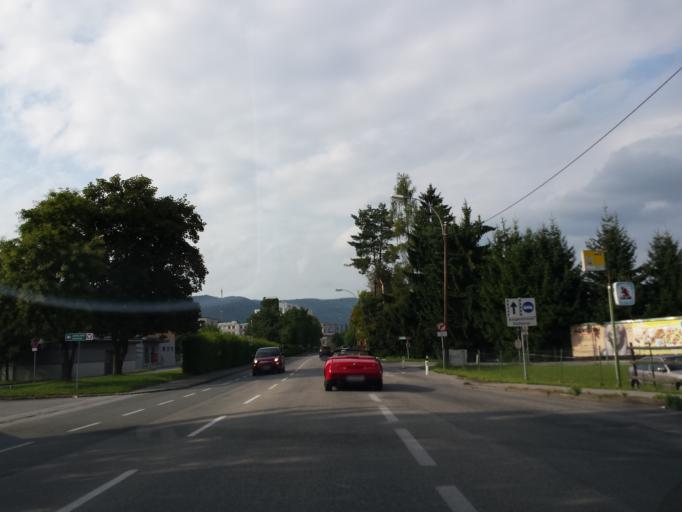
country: AT
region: Styria
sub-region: Graz Stadt
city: Wetzelsdorf
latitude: 47.0429
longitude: 15.3957
